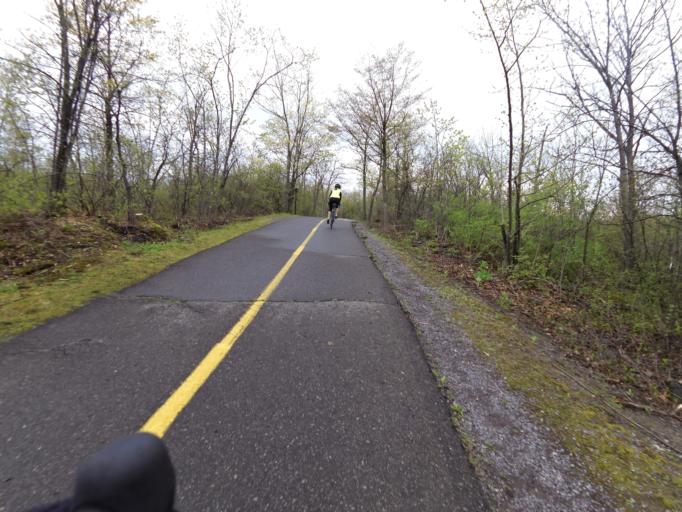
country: CA
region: Ontario
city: Ottawa
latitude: 45.4202
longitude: -75.7347
